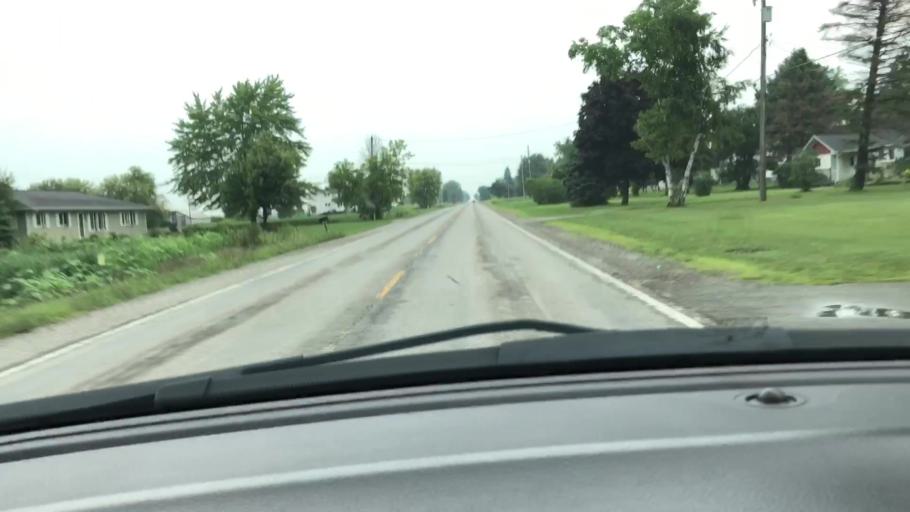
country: US
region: Michigan
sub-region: Saginaw County
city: Freeland
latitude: 43.5025
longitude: -84.0910
